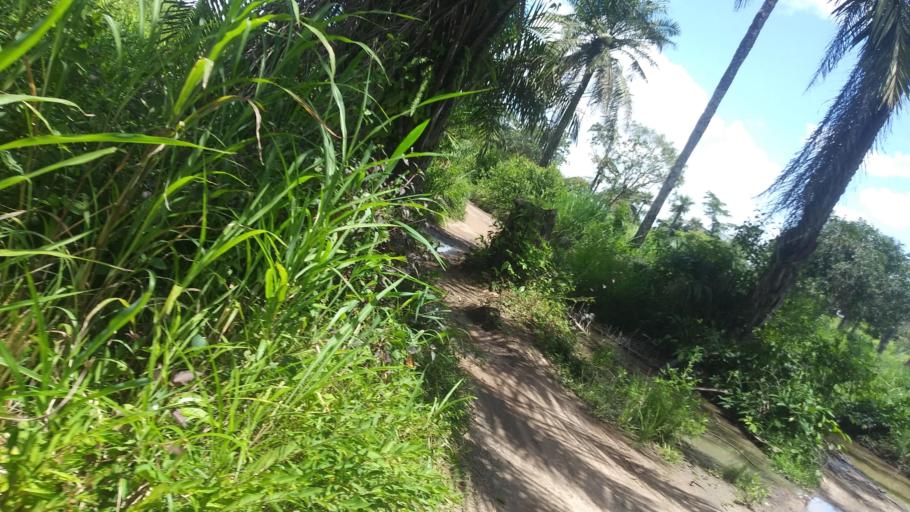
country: SL
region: Northern Province
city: Makeni
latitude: 8.8797
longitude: -12.0190
